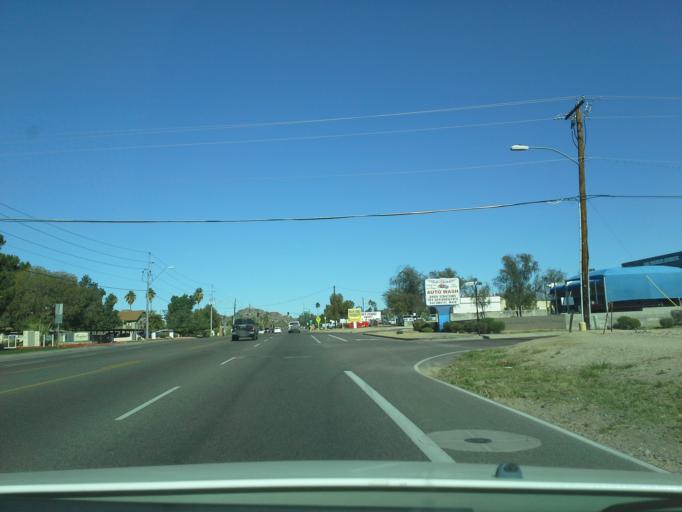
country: US
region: Arizona
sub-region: Maricopa County
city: Paradise Valley
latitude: 33.6456
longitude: -112.0308
